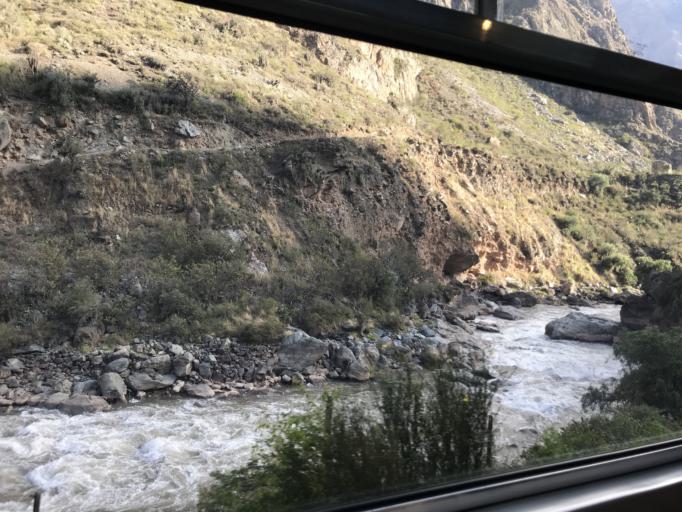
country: PE
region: Cusco
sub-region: Provincia de Urubamba
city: Ollantaytambo
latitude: -13.2158
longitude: -72.3848
